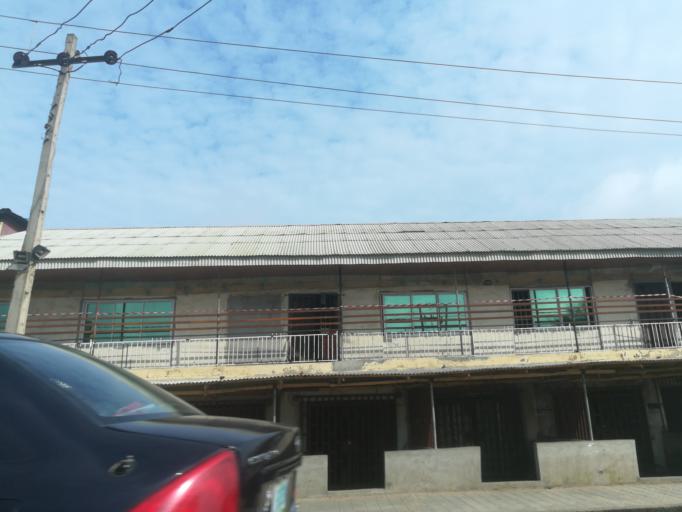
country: NG
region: Lagos
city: Agege
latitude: 6.6135
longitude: 3.3177
